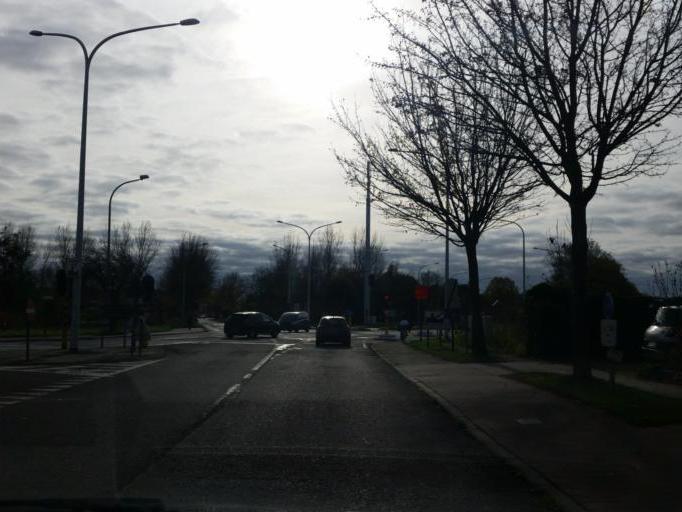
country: BE
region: Flanders
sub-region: Provincie Antwerpen
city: Edegem
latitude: 51.1460
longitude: 4.4465
